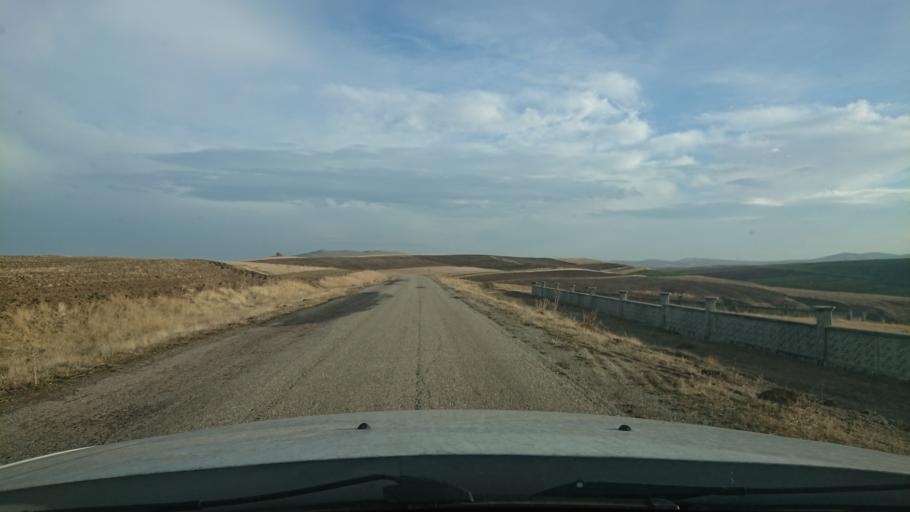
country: TR
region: Aksaray
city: Acipinar
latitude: 38.6634
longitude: 33.8455
